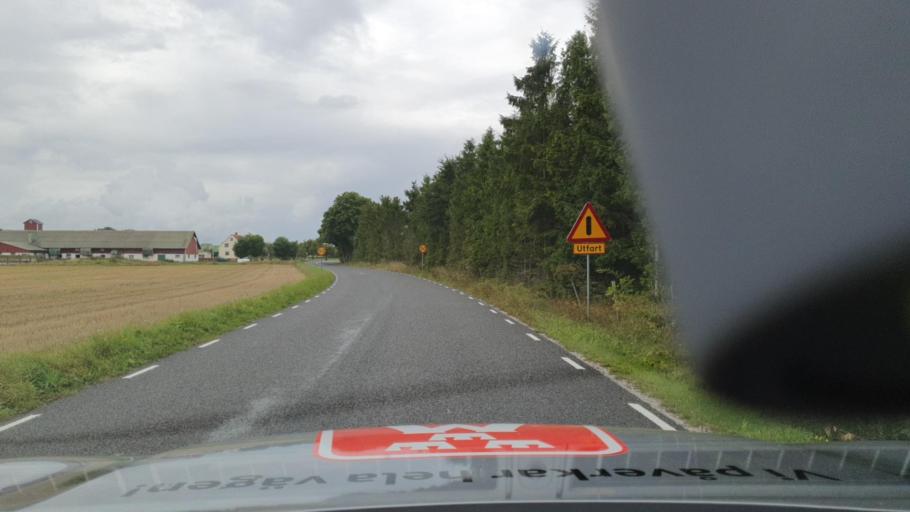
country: SE
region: Gotland
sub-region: Gotland
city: Visby
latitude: 57.5694
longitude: 18.4698
